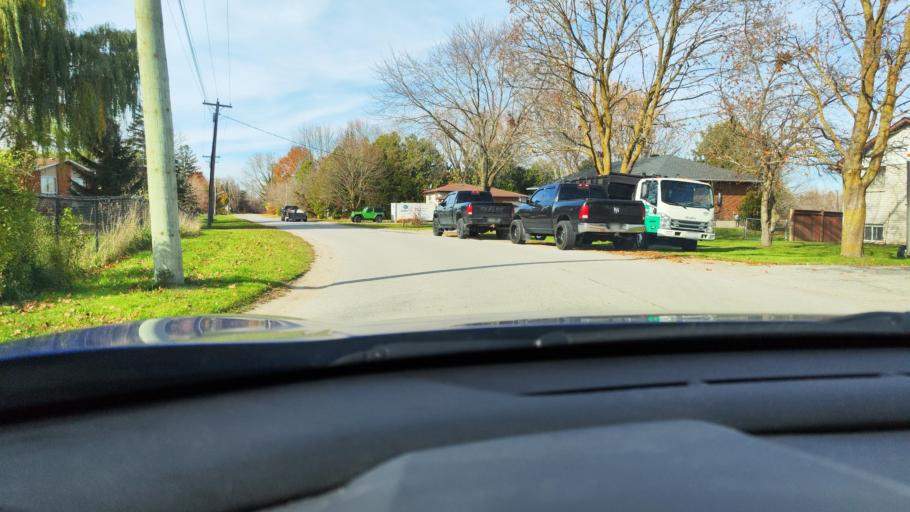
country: CA
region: Ontario
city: Angus
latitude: 44.3583
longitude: -79.9728
